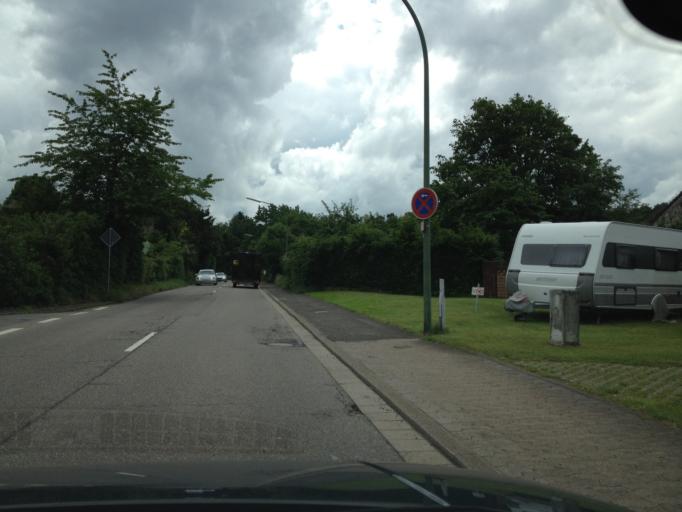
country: DE
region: Saarland
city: Bexbach
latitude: 49.3092
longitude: 7.2823
